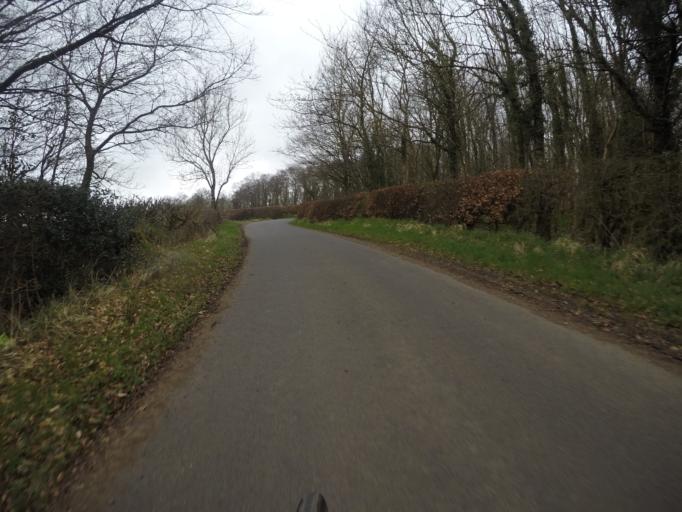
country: GB
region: Scotland
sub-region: East Ayrshire
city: Newmilns
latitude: 55.6178
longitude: -4.3541
